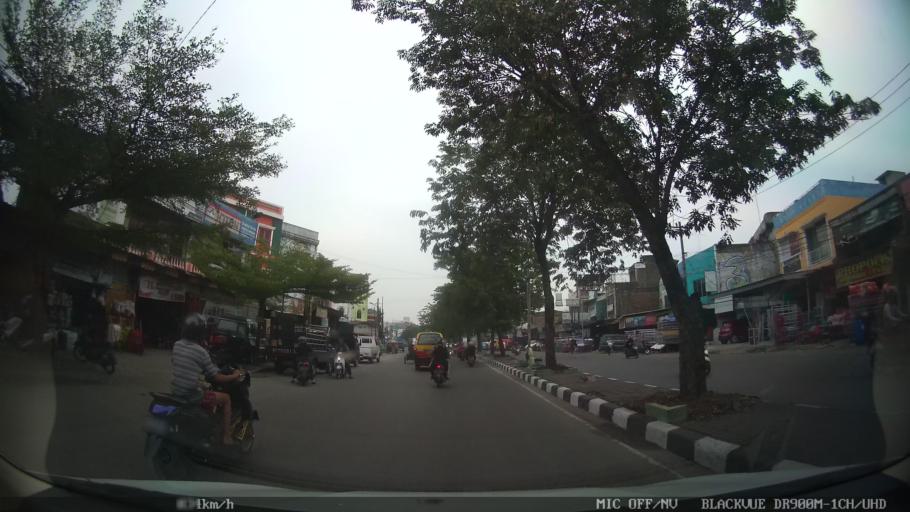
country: ID
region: North Sumatra
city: Medan
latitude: 3.5511
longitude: 98.6979
